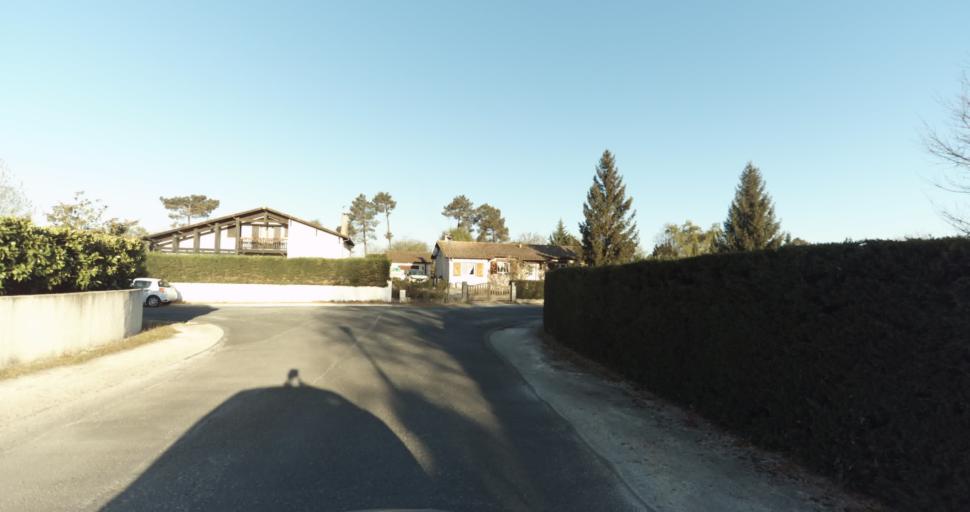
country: FR
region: Aquitaine
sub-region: Departement de la Gironde
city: Martignas-sur-Jalle
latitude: 44.8151
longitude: -0.7782
